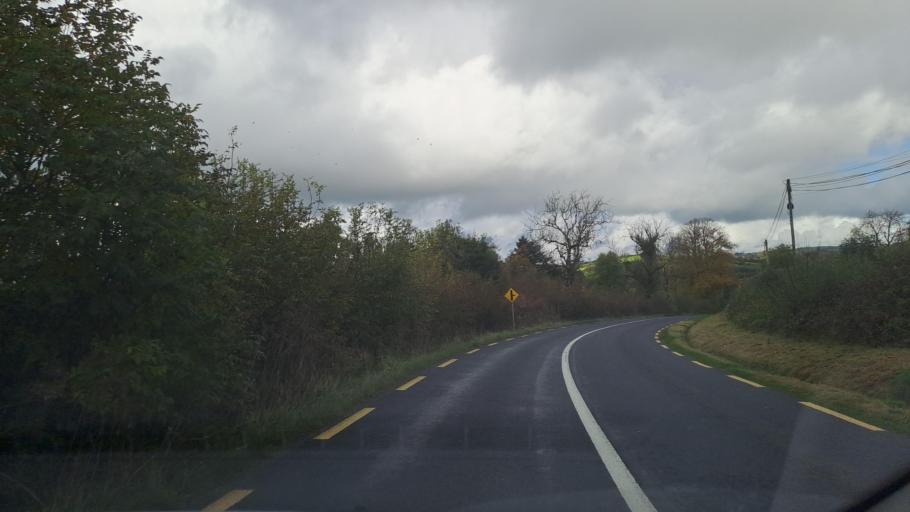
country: IE
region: Ulster
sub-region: An Cabhan
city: Bailieborough
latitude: 53.8852
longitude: -6.9643
